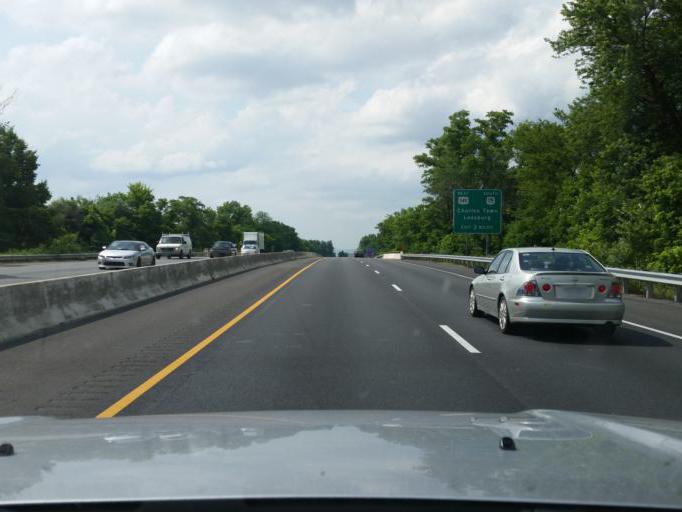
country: US
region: Maryland
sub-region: Frederick County
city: Ballenger Creek
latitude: 39.3679
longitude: -77.4017
